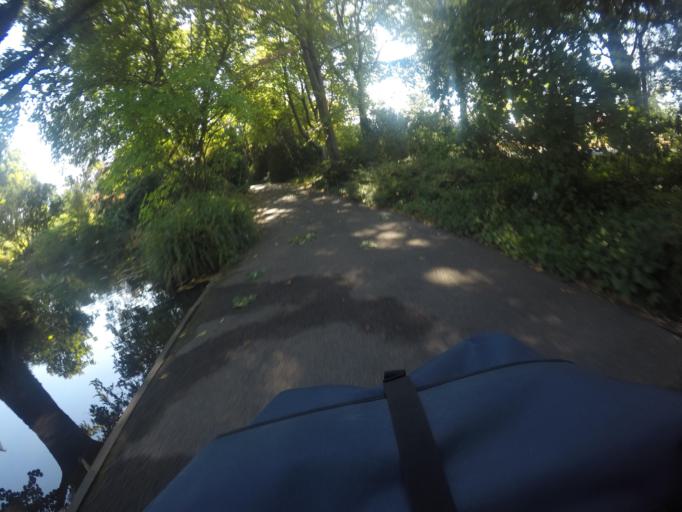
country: DE
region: North Rhine-Westphalia
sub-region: Regierungsbezirk Koln
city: Leverkusen
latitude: 51.0114
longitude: 6.9809
